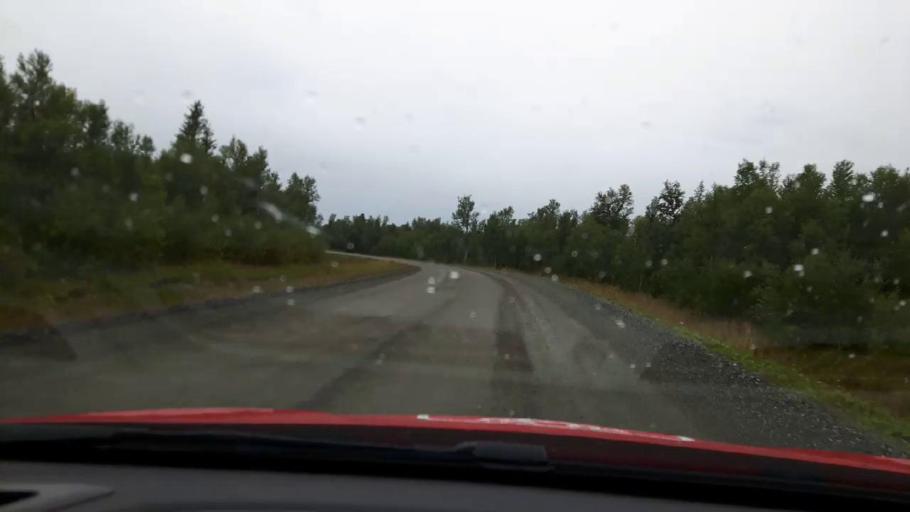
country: NO
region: Nord-Trondelag
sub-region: Meraker
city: Meraker
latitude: 63.5831
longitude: 12.2673
